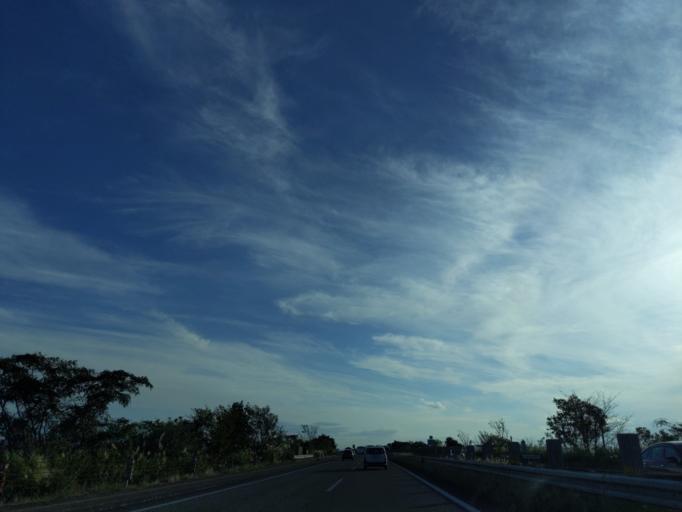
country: JP
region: Niigata
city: Sanjo
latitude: 37.6002
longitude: 138.9016
